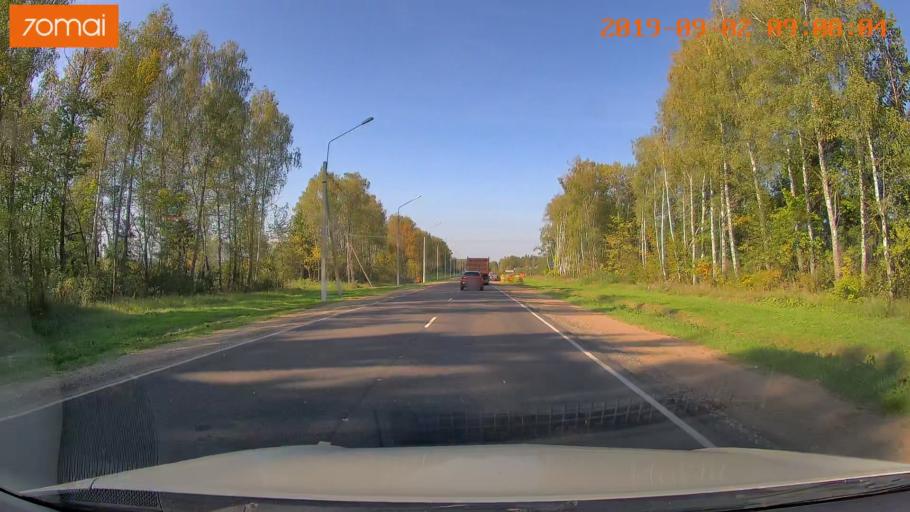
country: RU
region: Kaluga
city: Myatlevo
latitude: 54.8922
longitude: 35.6473
